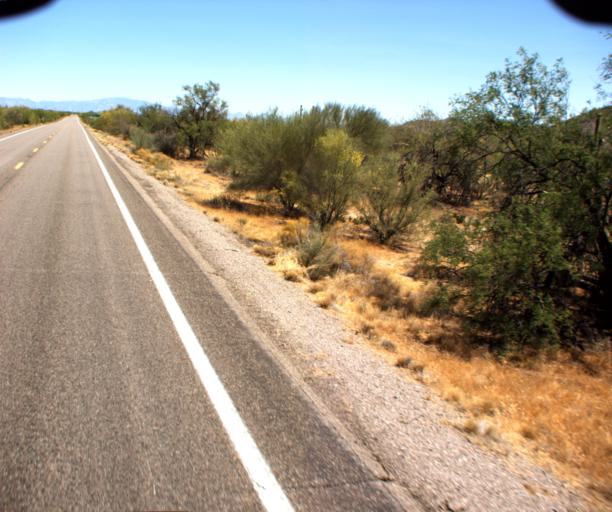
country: US
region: Arizona
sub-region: Pima County
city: Marana
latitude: 32.7601
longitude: -111.1456
